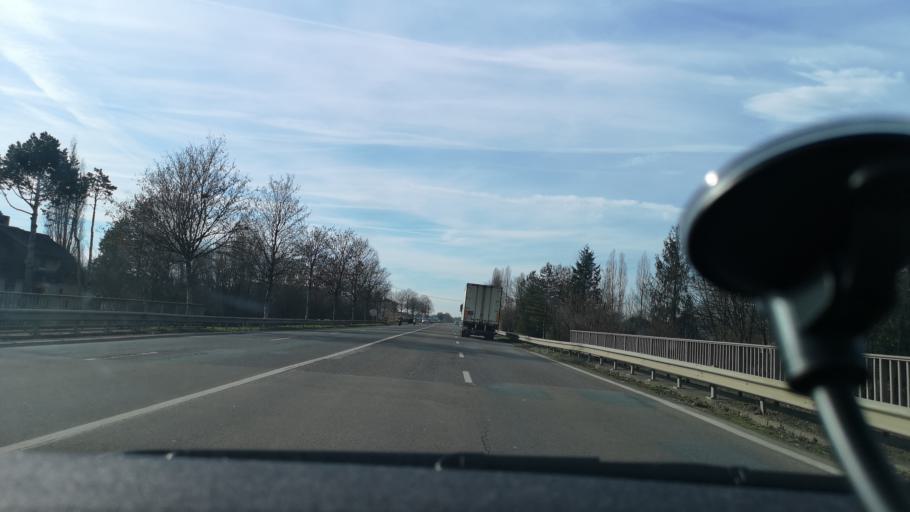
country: FR
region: Franche-Comte
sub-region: Departement du Doubs
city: Dannemarie-sur-Crete
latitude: 47.2008
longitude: 5.8745
